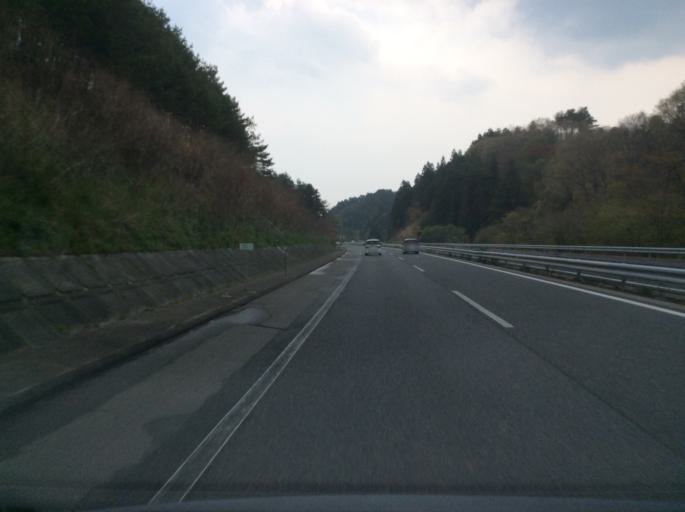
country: JP
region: Fukushima
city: Iwaki
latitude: 37.1862
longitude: 140.7099
